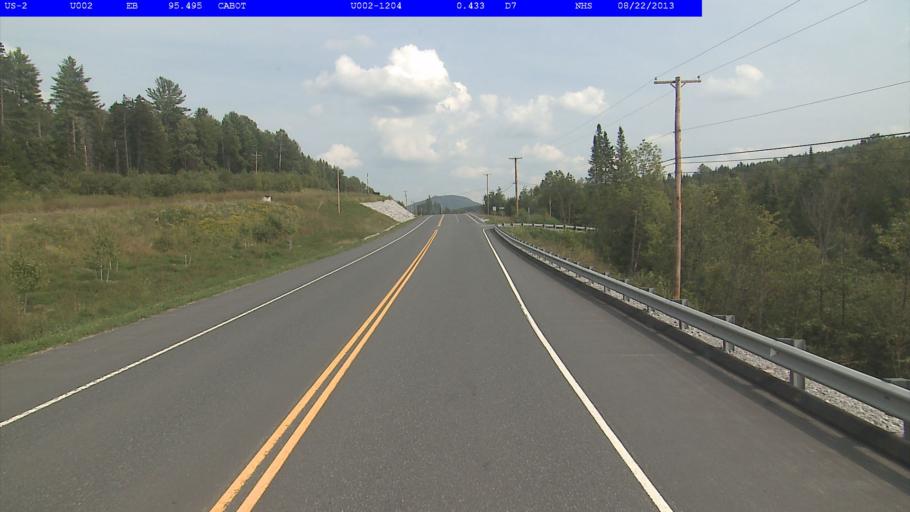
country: US
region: Vermont
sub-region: Caledonia County
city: Hardwick
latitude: 44.3637
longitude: -72.3159
